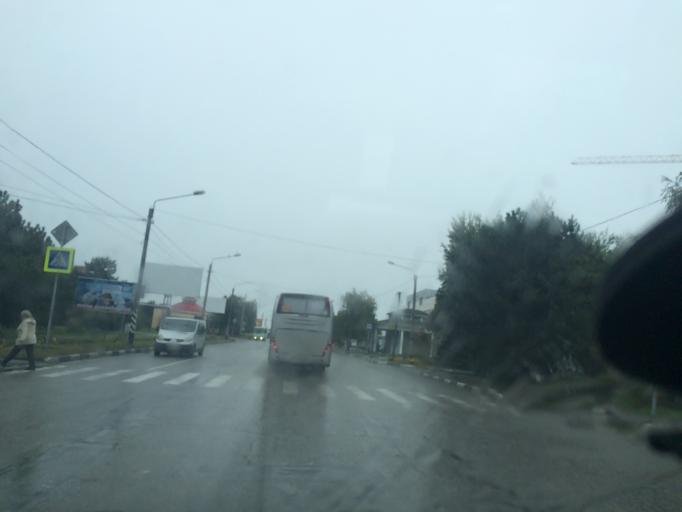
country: RU
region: Rostov
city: Azov
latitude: 47.0921
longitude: 39.4514
